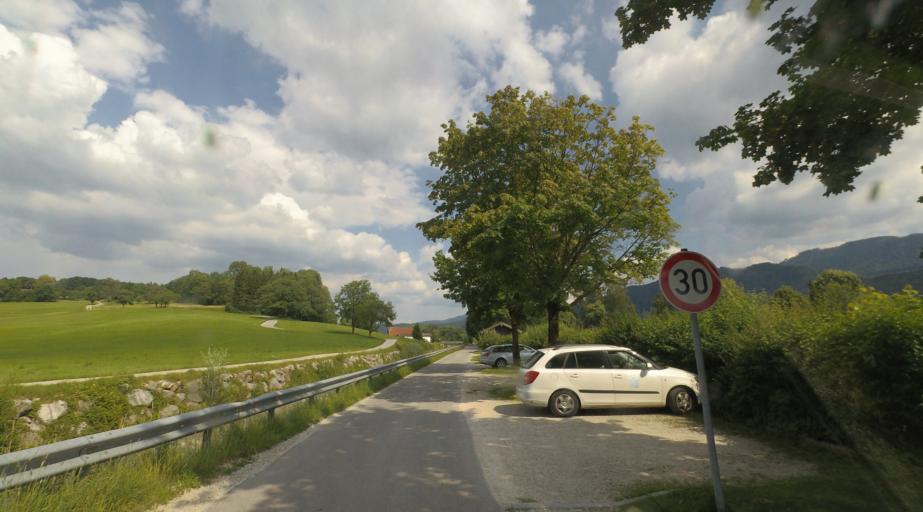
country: DE
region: Bavaria
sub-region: Upper Bavaria
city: Bergen
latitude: 47.8087
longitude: 12.5734
